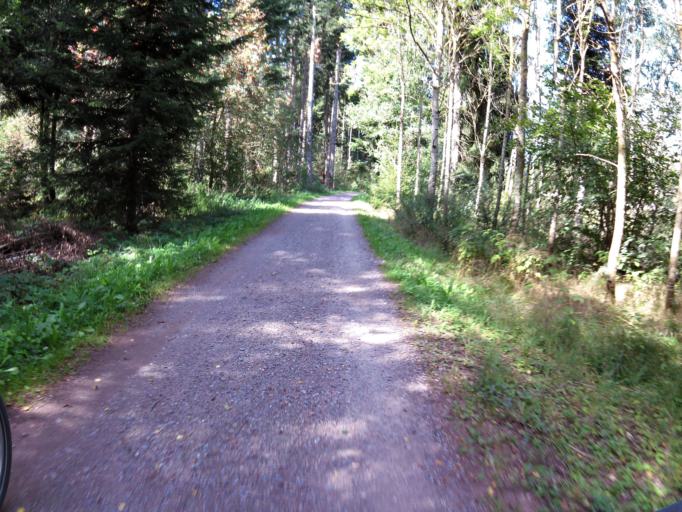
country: DE
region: Baden-Wuerttemberg
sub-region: Freiburg Region
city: Bad Durrheim
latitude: 48.0443
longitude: 8.5178
